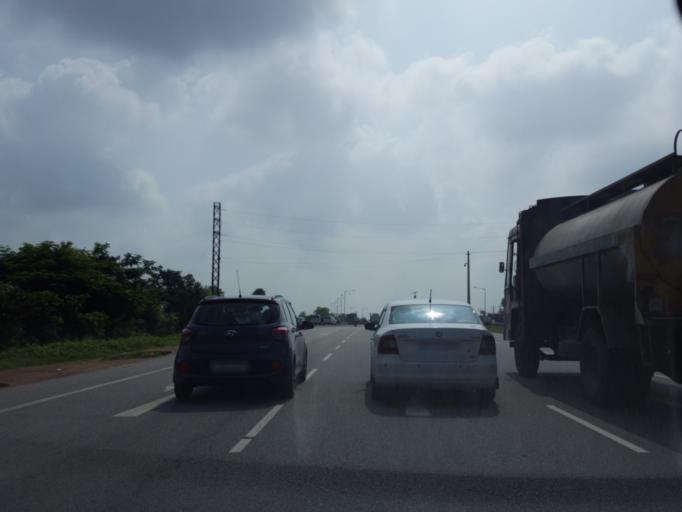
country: IN
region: Telangana
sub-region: Nalgonda
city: Gudur
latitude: 17.2741
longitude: 78.8154
